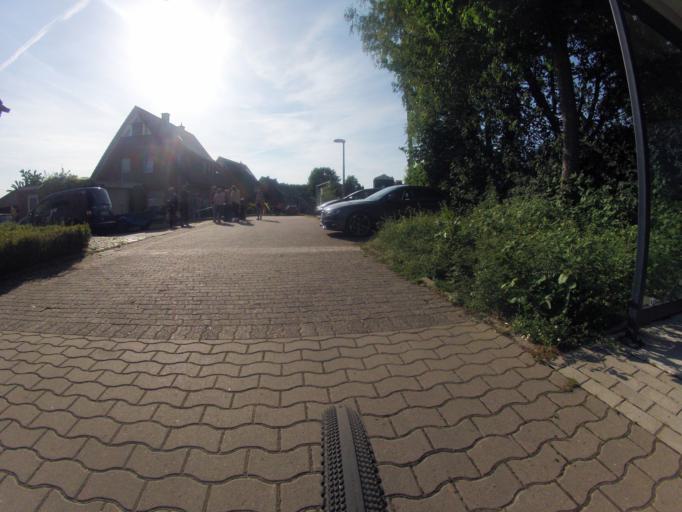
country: DE
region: North Rhine-Westphalia
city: Ibbenburen
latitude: 52.2928
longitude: 7.7048
